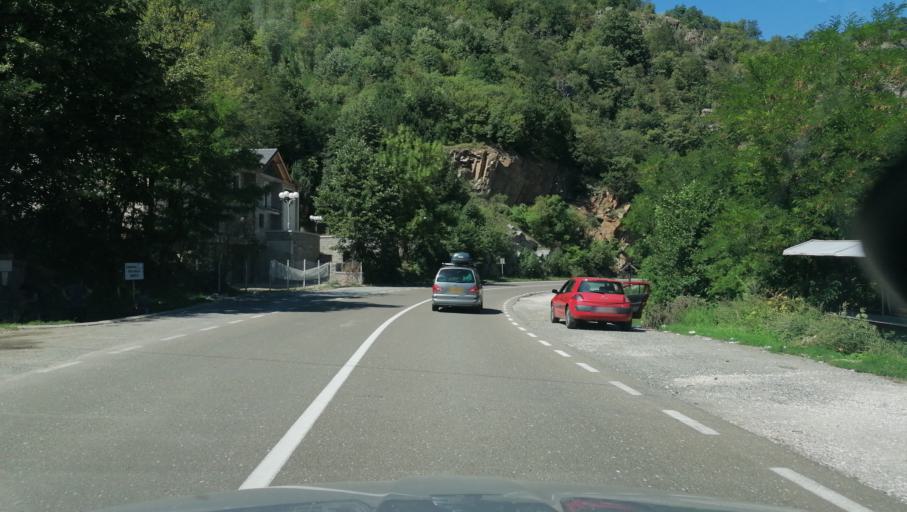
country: RS
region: Central Serbia
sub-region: Raski Okrug
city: Raska
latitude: 43.5017
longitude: 20.6155
